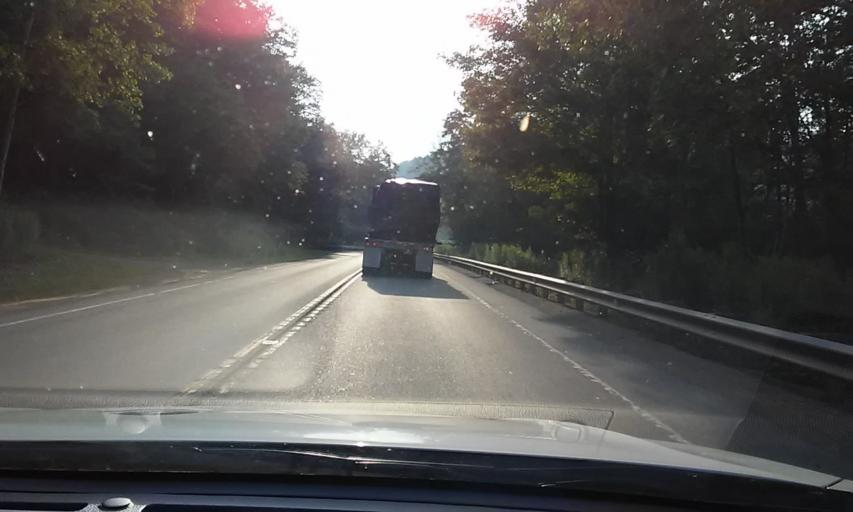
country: US
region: Pennsylvania
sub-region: McKean County
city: Smethport
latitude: 41.7050
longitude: -78.5895
